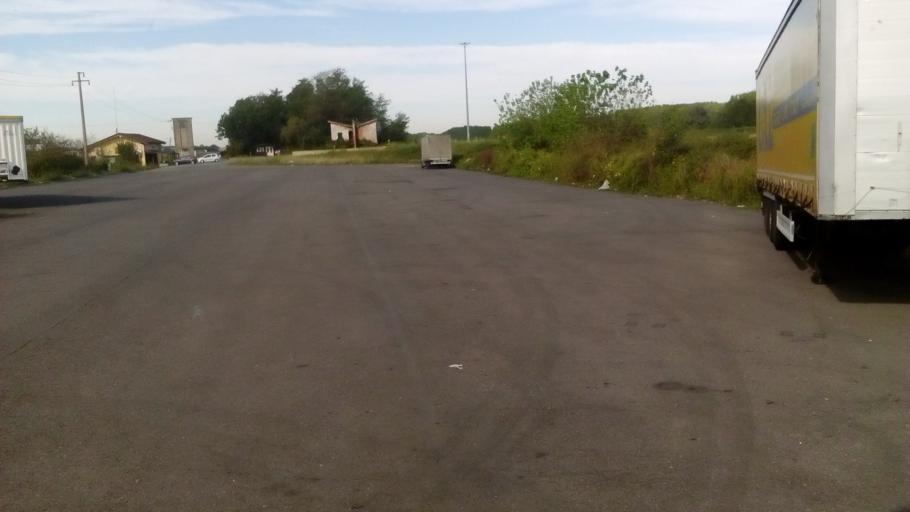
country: IT
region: Lombardy
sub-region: Provincia di Pavia
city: Miradolo Terme
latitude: 45.1599
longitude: 9.4251
